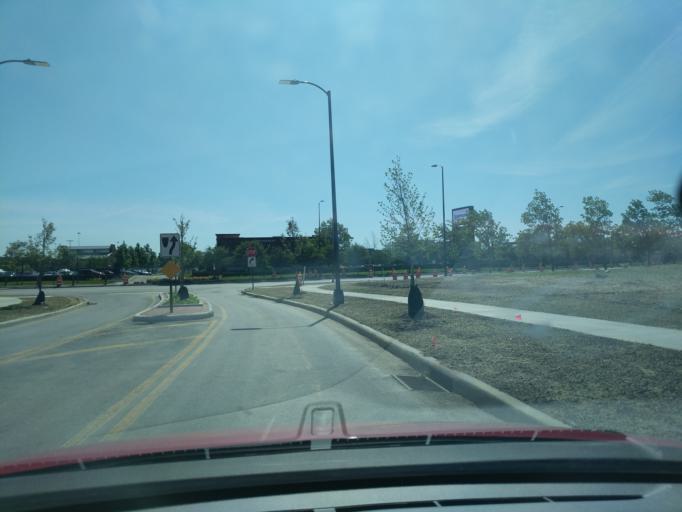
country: US
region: Ohio
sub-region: Franklin County
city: Huber Ridge
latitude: 40.0560
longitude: -82.9112
